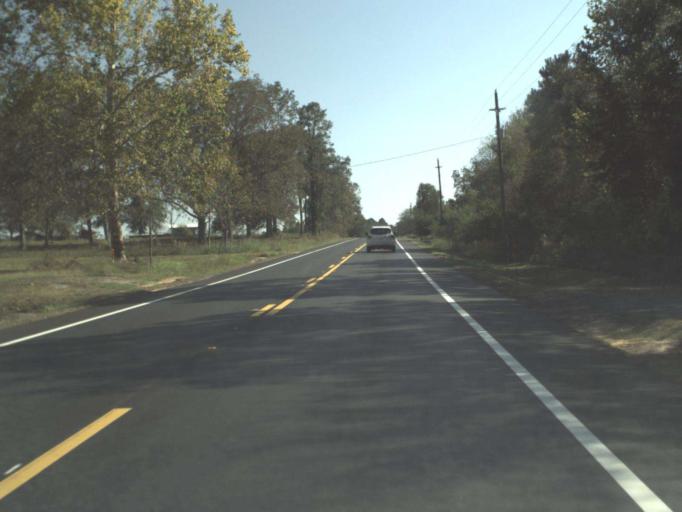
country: US
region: Alabama
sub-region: Covington County
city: Florala
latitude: 30.9361
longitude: -86.2816
